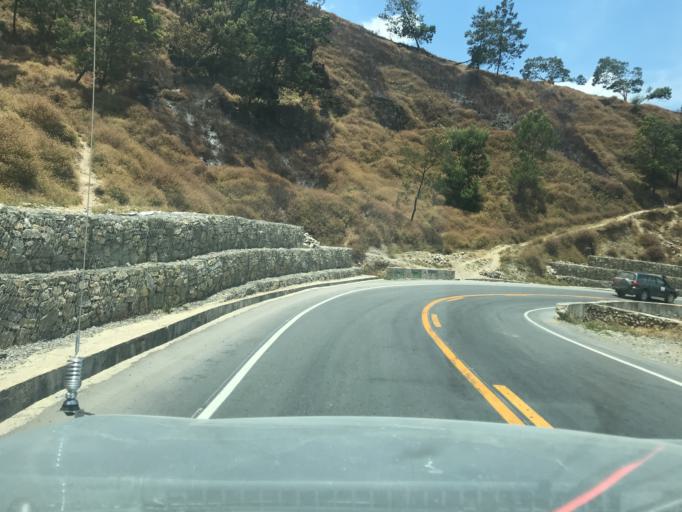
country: TL
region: Manufahi
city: Same
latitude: -8.8825
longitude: 125.6062
